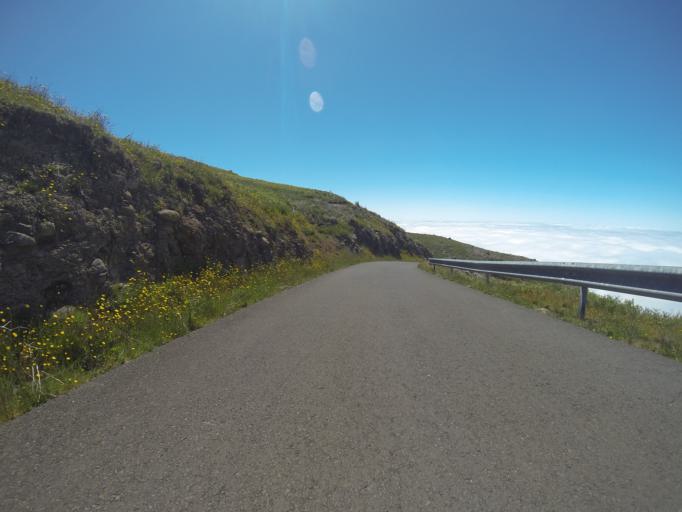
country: PT
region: Madeira
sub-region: Funchal
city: Nossa Senhora do Monte
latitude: 32.7067
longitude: -16.9150
